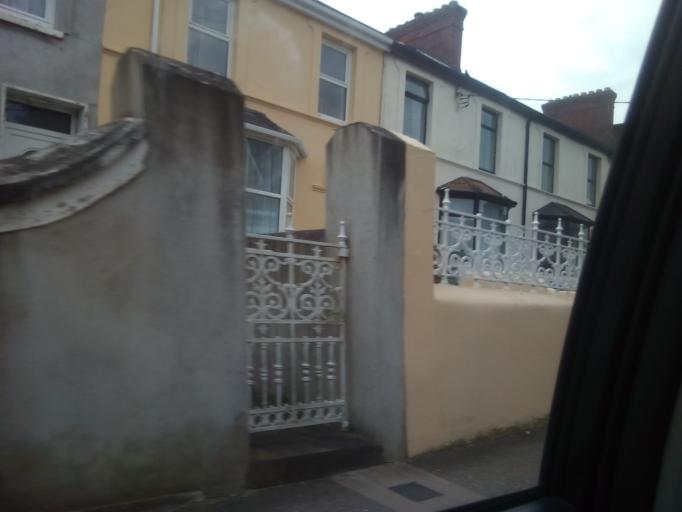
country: IE
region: Munster
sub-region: County Cork
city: Cork
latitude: 51.8896
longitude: -8.4950
